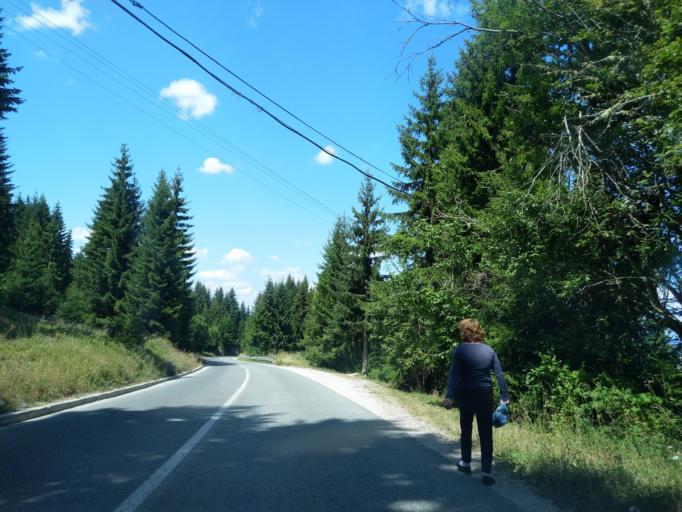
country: RS
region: Central Serbia
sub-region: Zlatiborski Okrug
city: Nova Varos
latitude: 43.4108
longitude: 19.8374
